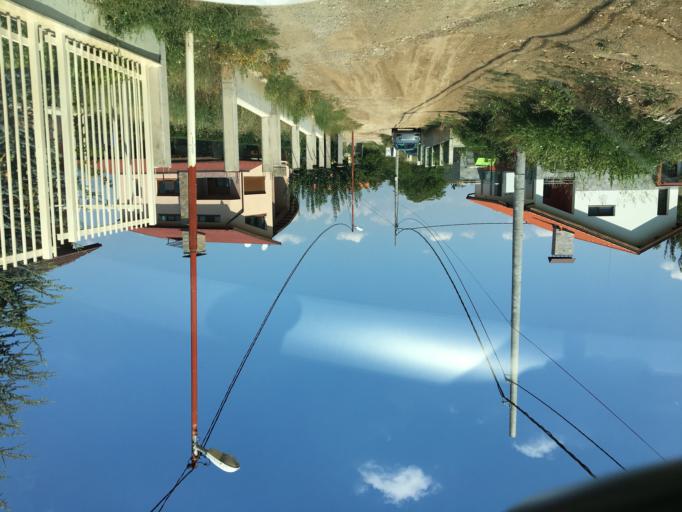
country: BG
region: Sofiya
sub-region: Obshtina Elin Pelin
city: Elin Pelin
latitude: 42.6031
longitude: 23.4672
